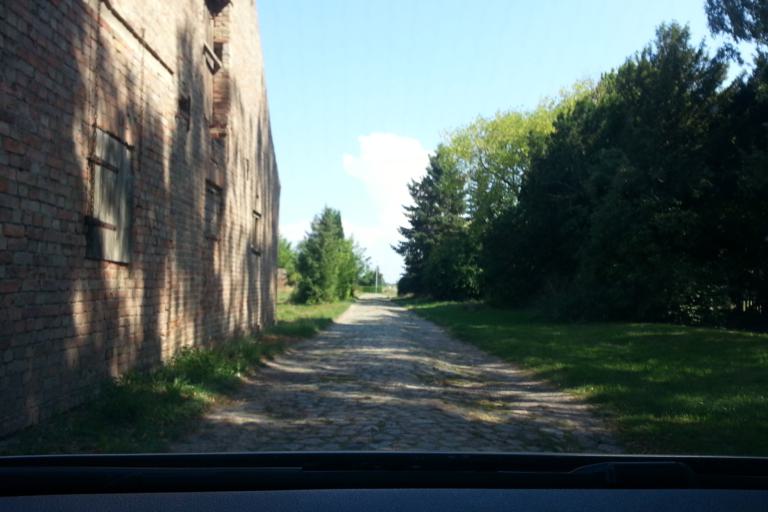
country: DE
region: Mecklenburg-Vorpommern
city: Ducherow
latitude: 53.7128
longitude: 13.7897
